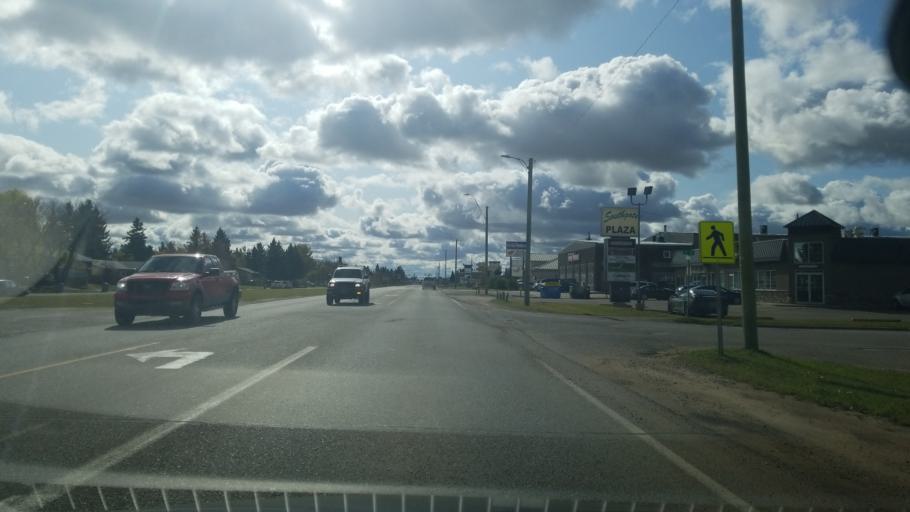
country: CA
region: Saskatchewan
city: Lloydminster
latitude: 53.2755
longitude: -110.0052
